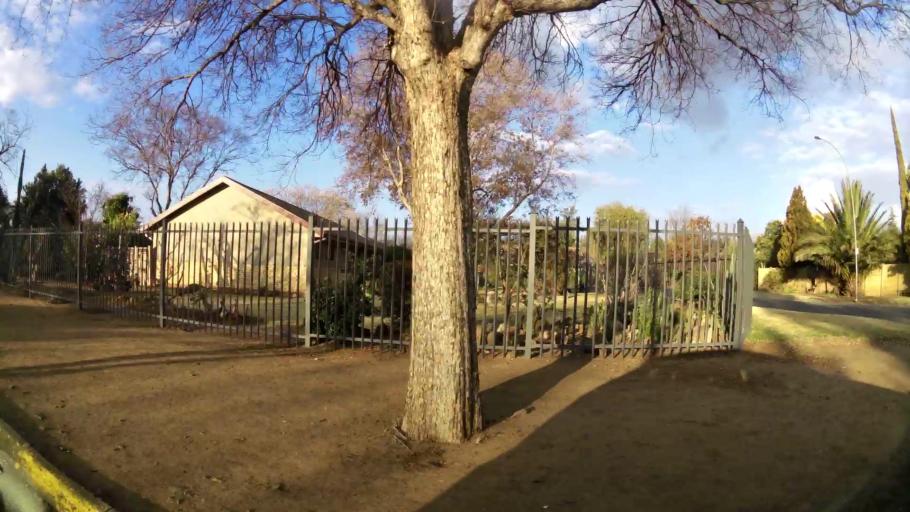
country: ZA
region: Orange Free State
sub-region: Mangaung Metropolitan Municipality
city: Bloemfontein
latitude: -29.1345
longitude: 26.1910
